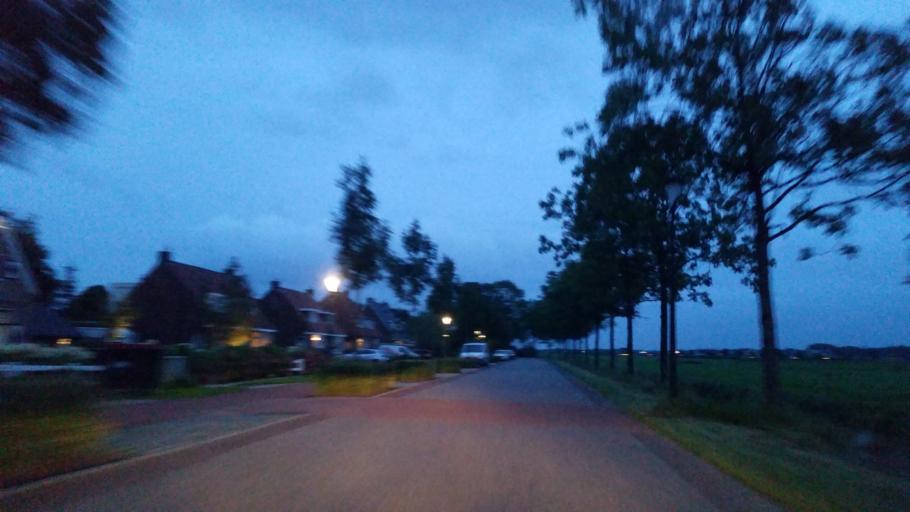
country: NL
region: Friesland
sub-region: Gemeente Leeuwarden
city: Bilgaard
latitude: 53.2231
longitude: 5.8178
